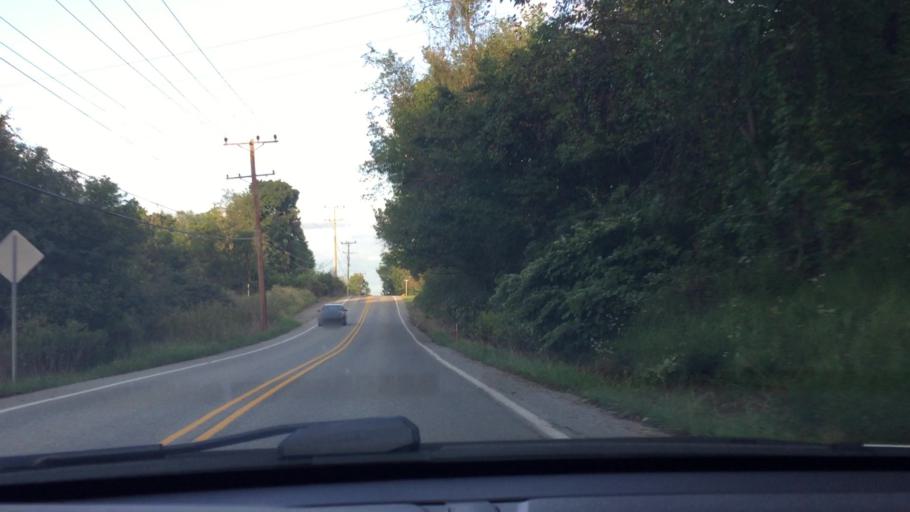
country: US
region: Pennsylvania
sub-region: Allegheny County
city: Plum
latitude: 40.4571
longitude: -79.7429
